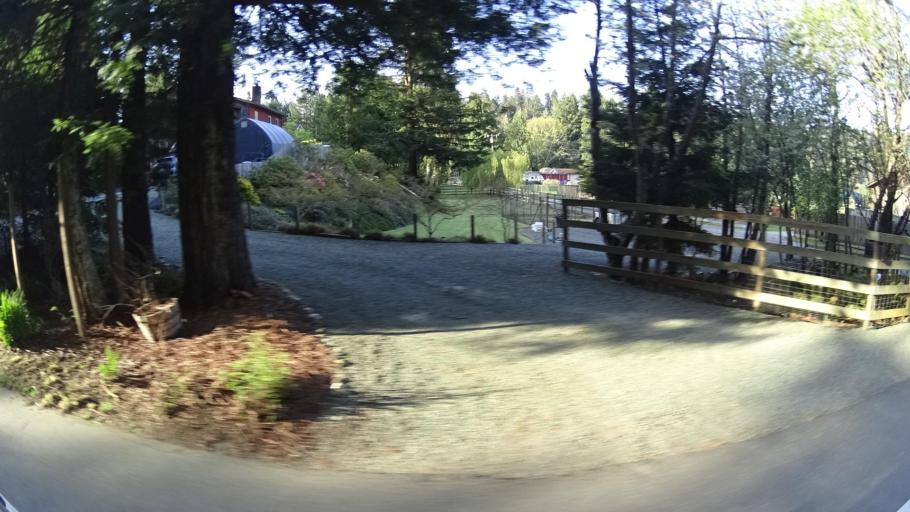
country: US
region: California
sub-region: Humboldt County
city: Myrtletown
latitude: 40.7603
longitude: -124.0579
